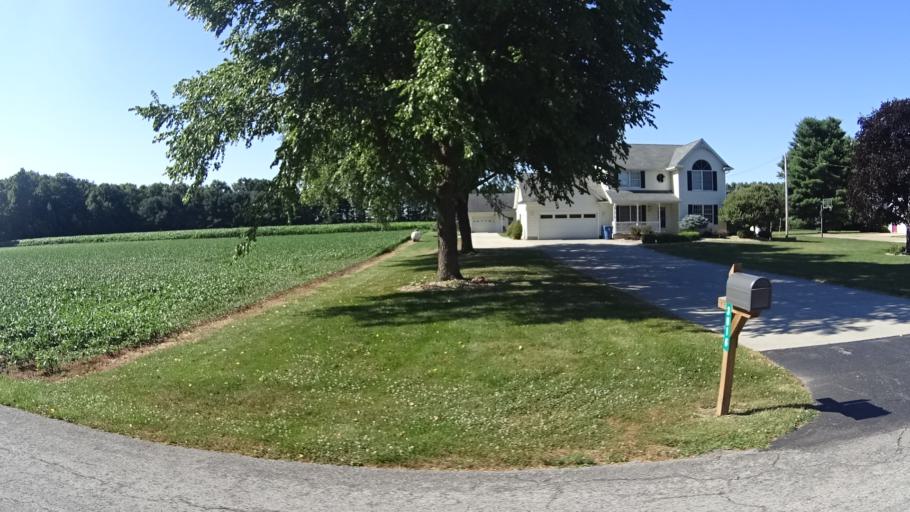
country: US
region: Ohio
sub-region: Erie County
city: Sandusky
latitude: 41.3731
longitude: -82.7377
